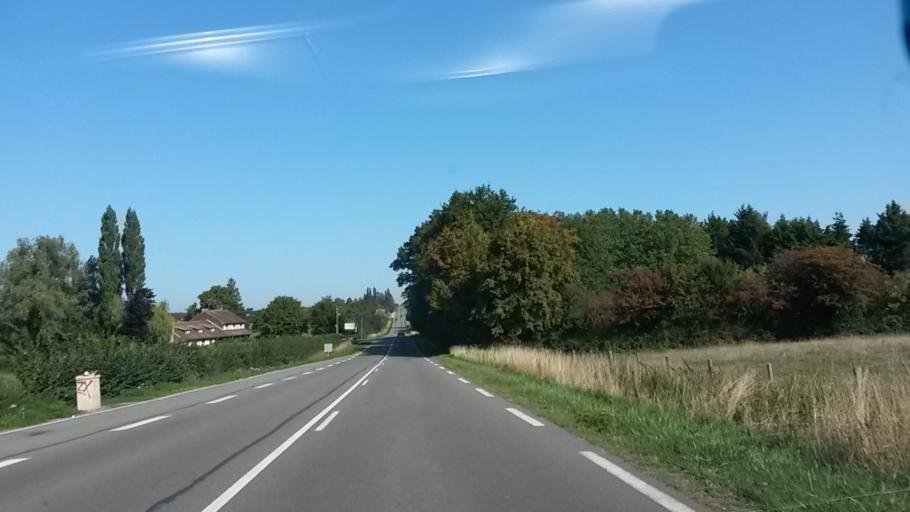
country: FR
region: Nord-Pas-de-Calais
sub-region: Departement du Nord
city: Avesnelles
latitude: 50.1634
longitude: 3.9540
